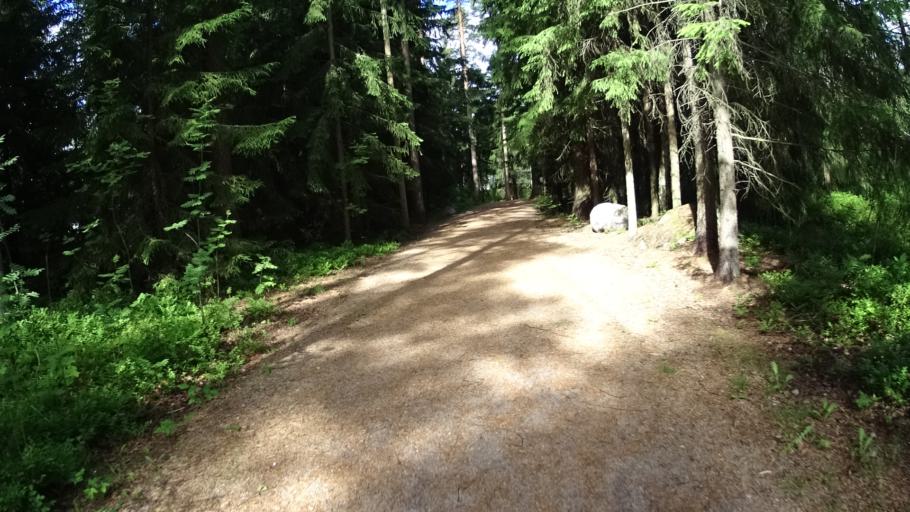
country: FI
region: Uusimaa
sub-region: Helsinki
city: Otaniemi
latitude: 60.1962
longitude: 24.8019
